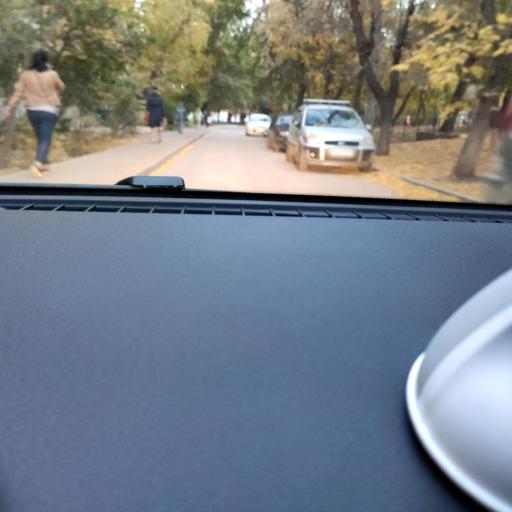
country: RU
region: Samara
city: Samara
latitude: 53.2132
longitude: 50.1349
